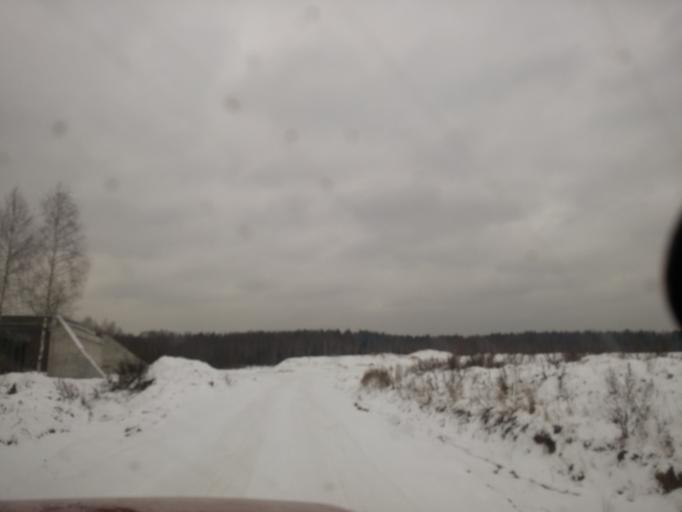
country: RU
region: Moskovskaya
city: Reshetnikovo
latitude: 56.4605
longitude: 36.5426
